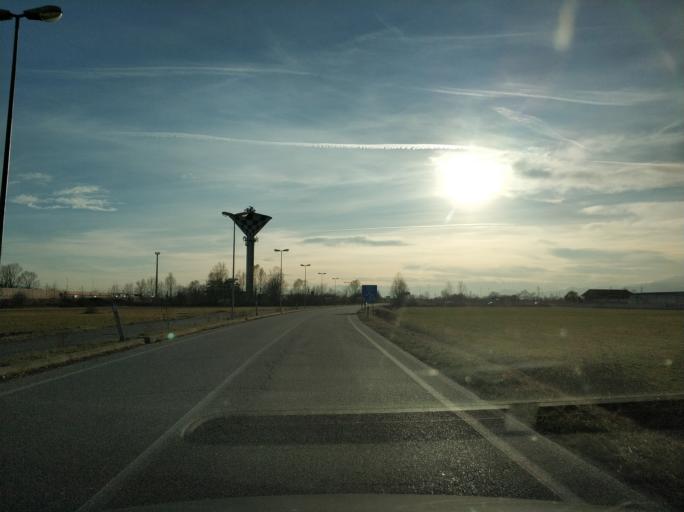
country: IT
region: Piedmont
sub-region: Provincia di Torino
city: Brandizzo
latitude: 45.1850
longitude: 7.8324
